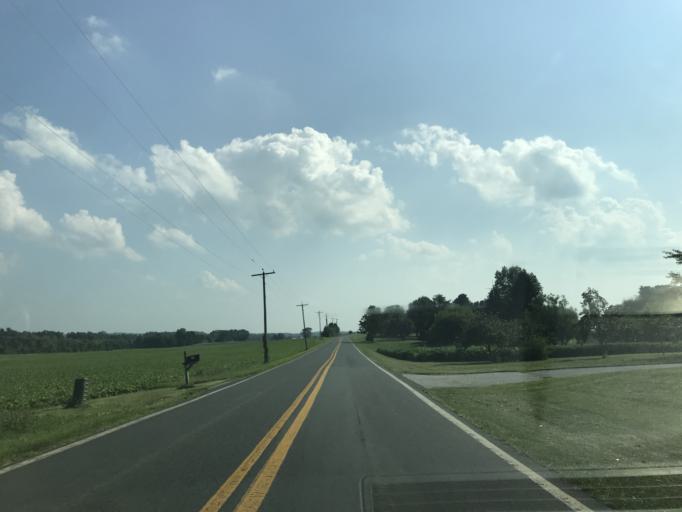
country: US
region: Maryland
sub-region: Carroll County
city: Westminster
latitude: 39.6252
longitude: -76.9722
